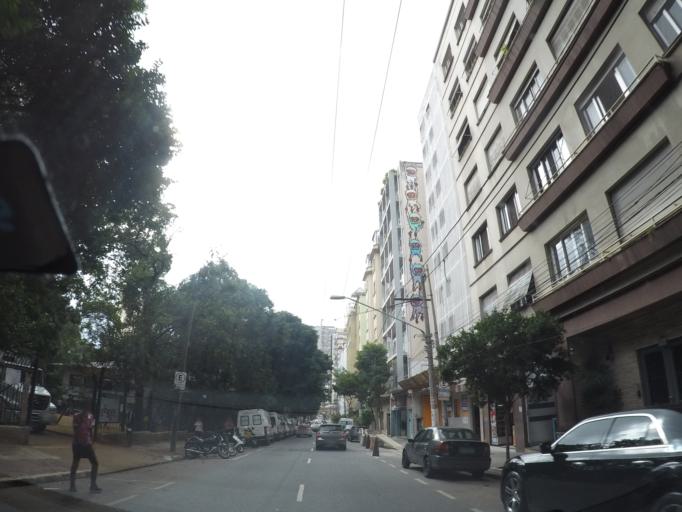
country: BR
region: Sao Paulo
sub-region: Sao Paulo
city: Sao Paulo
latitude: -23.5454
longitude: -46.6501
